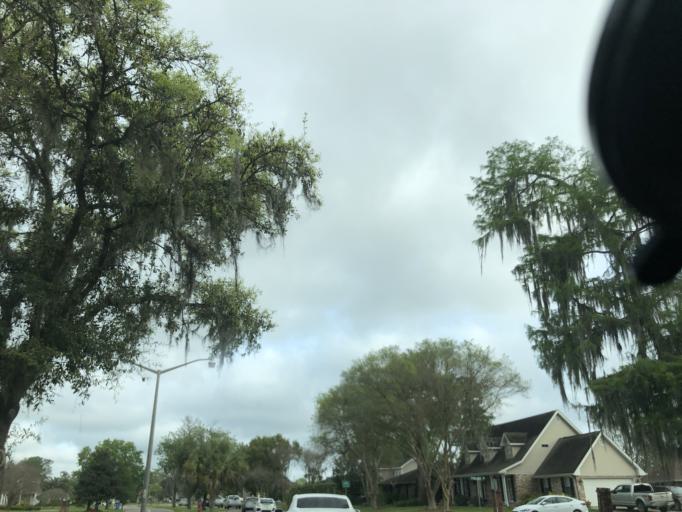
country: US
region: Louisiana
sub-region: Saint Charles Parish
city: New Sarpy
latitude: 29.9812
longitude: -90.3628
